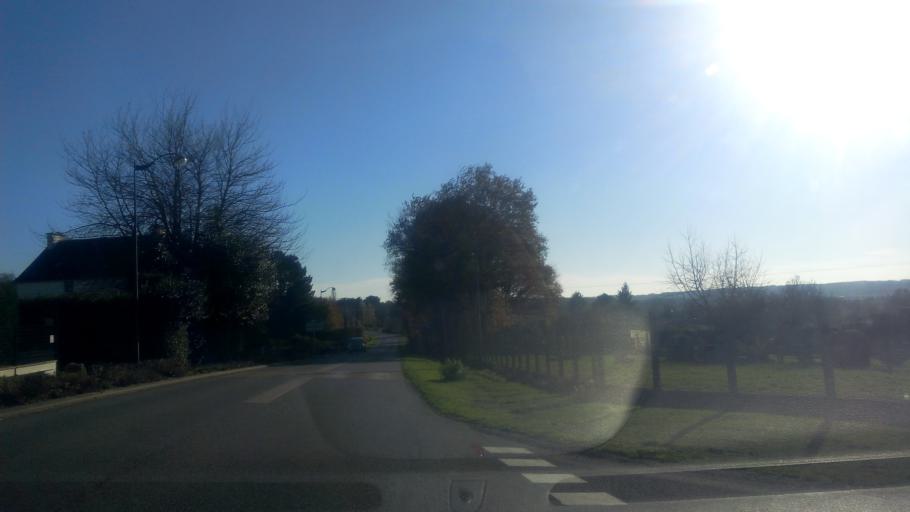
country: FR
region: Brittany
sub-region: Departement du Morbihan
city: Saint-Vincent-sur-Oust
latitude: 47.6960
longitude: -2.1445
